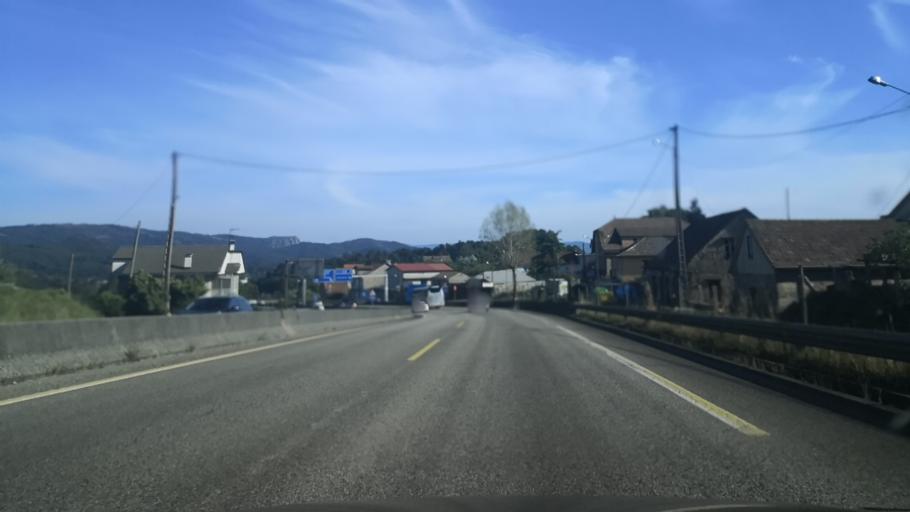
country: ES
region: Galicia
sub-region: Provincia de Pontevedra
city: Porrino
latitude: 42.1885
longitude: -8.6385
